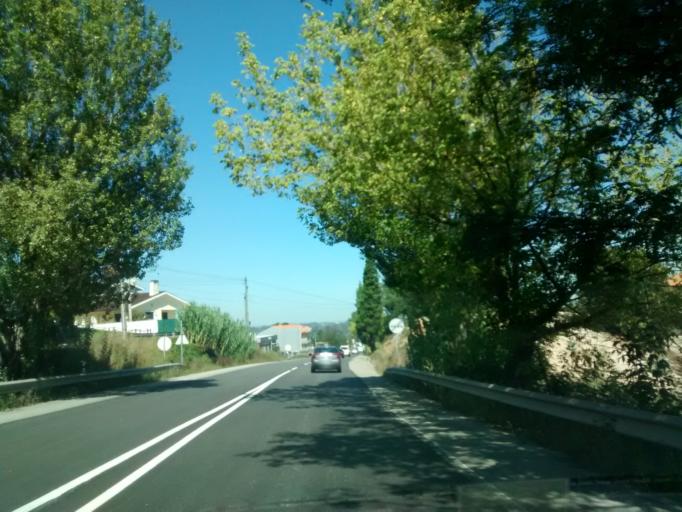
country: PT
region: Aveiro
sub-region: Oliveira do Bairro
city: Oia
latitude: 40.5484
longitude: -8.5399
